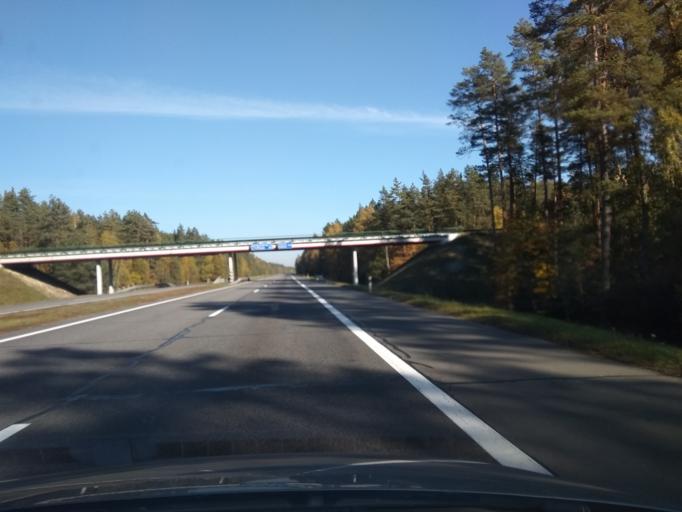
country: BY
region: Brest
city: Baranovichi
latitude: 53.0345
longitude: 25.8130
